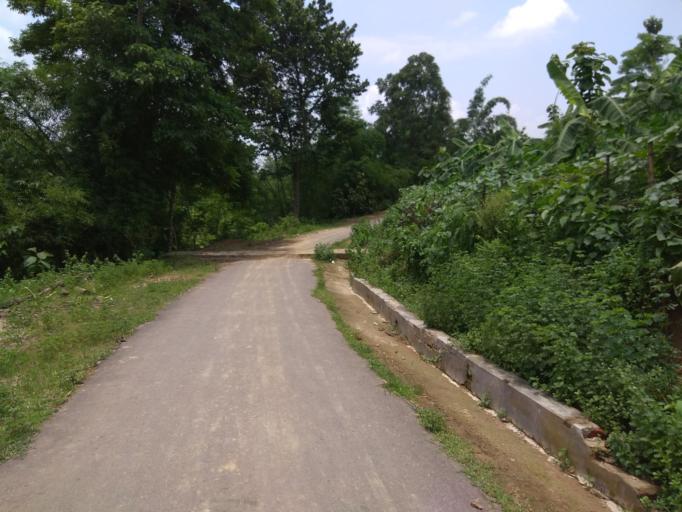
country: BD
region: Chittagong
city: Manikchari
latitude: 22.8880
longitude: 91.9224
